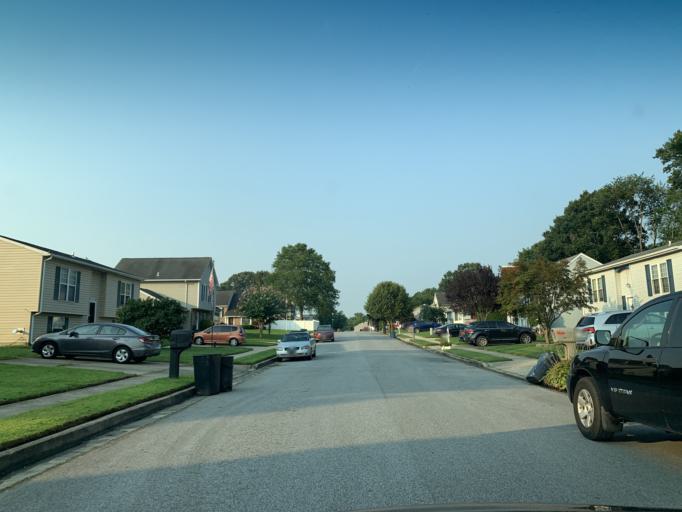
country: US
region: Maryland
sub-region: Baltimore County
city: Bowleys Quarters
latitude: 39.3664
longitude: -76.3612
